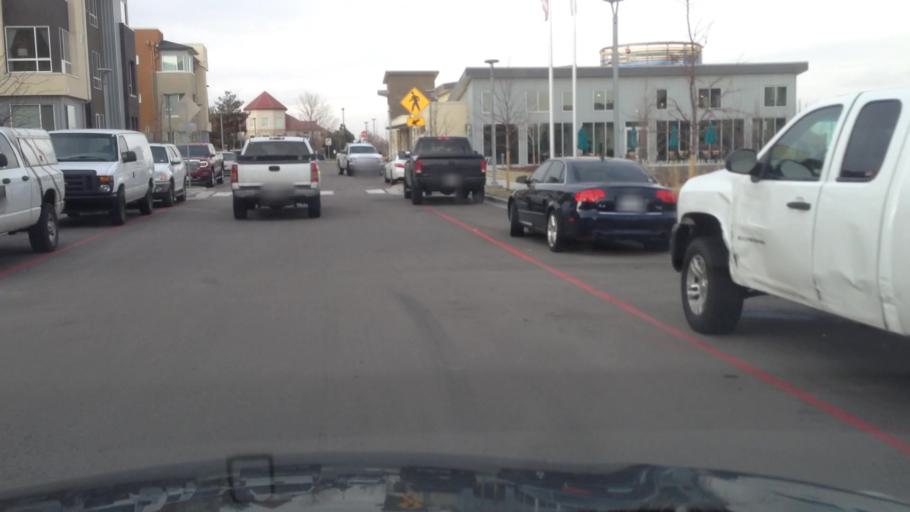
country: US
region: Colorado
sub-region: Adams County
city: Aurora
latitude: 39.6692
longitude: -104.8246
